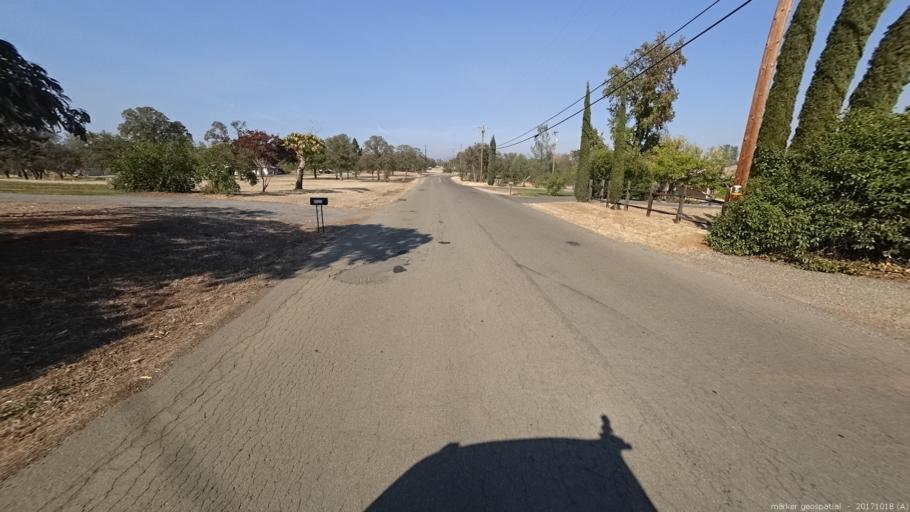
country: US
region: California
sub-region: Shasta County
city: Palo Cedro
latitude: 40.5561
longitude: -122.2767
